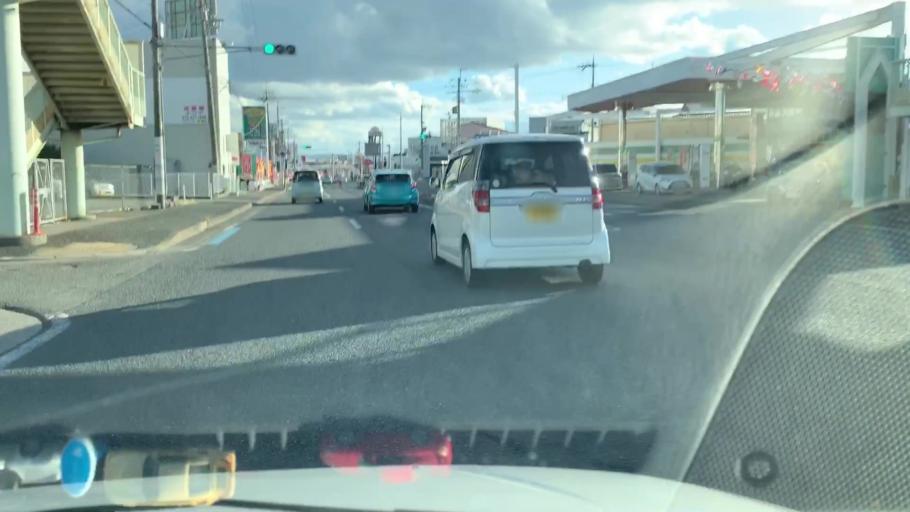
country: JP
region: Wakayama
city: Wakayama-shi
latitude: 34.2468
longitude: 135.1503
